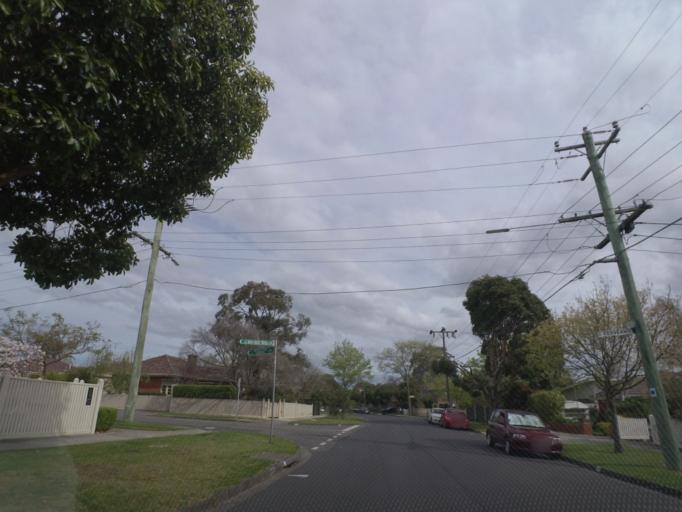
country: AU
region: Victoria
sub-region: Whitehorse
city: Surrey Hills
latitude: -37.8298
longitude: 145.1042
